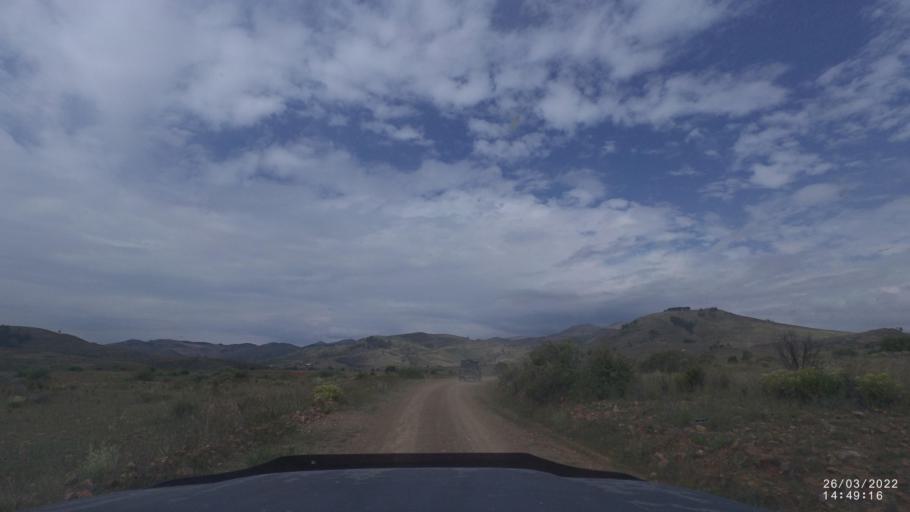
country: BO
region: Cochabamba
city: Cliza
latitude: -17.7260
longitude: -65.8529
